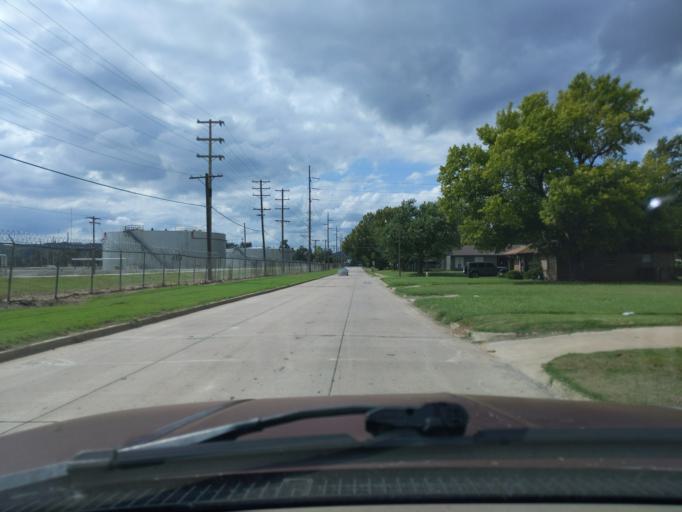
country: US
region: Oklahoma
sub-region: Tulsa County
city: Tulsa
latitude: 36.1263
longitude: -96.0025
